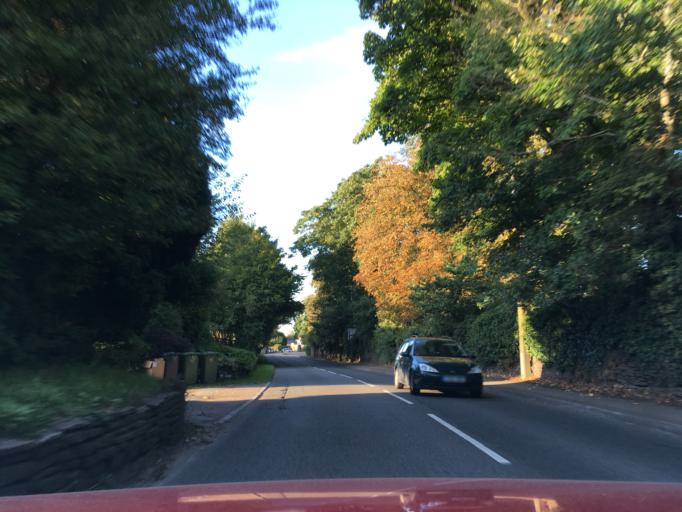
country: GB
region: England
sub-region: South Gloucestershire
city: Winterbourne
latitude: 51.5071
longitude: -2.5191
